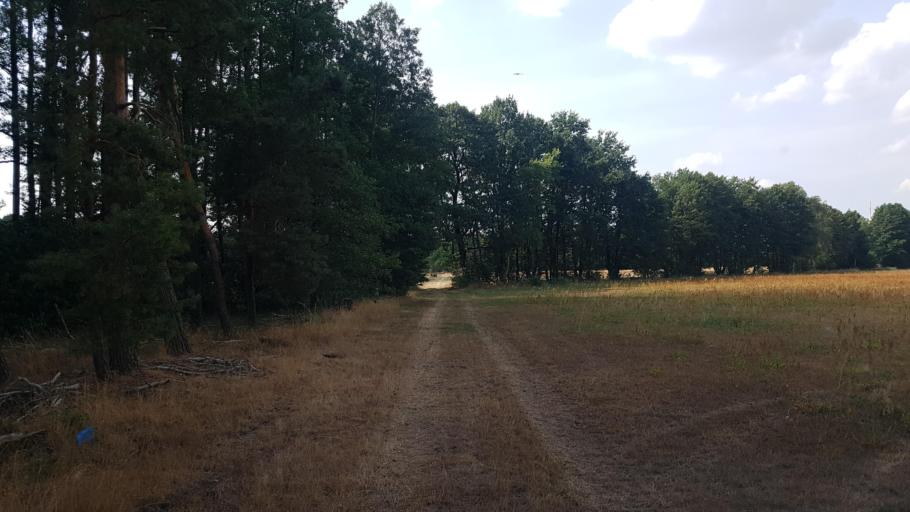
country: DE
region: Brandenburg
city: Finsterwalde
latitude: 51.6573
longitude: 13.7488
